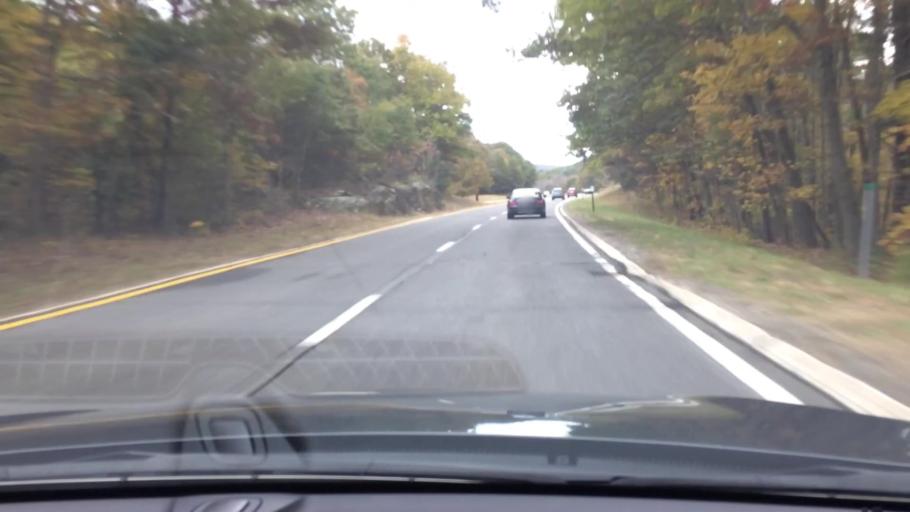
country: US
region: New York
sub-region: Dutchess County
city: Pine Plains
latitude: 42.0397
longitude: -73.7341
